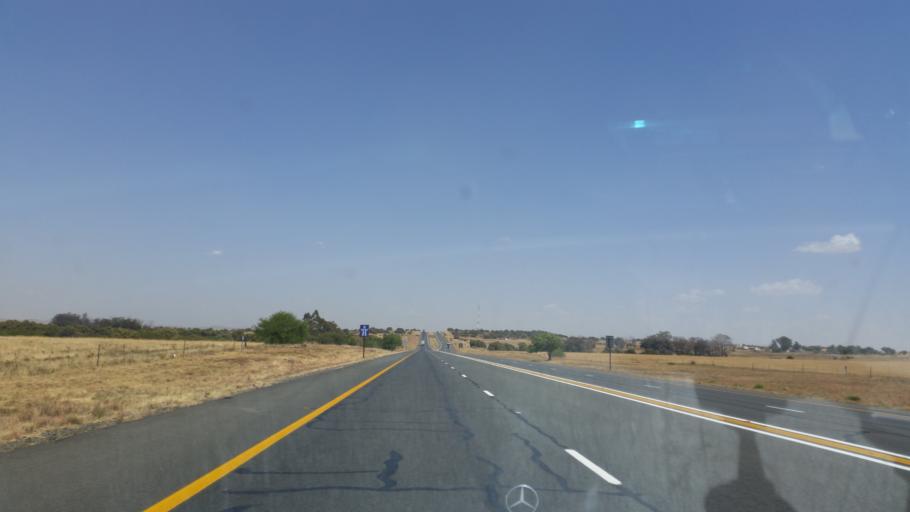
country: ZA
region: Orange Free State
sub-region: Lejweleputswa District Municipality
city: Brandfort
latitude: -28.9001
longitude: 26.4706
